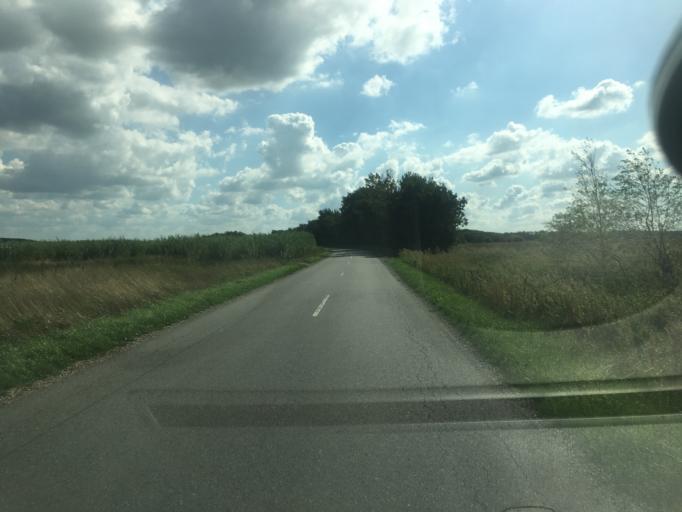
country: DE
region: Schleswig-Holstein
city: Ellhoft
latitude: 54.9643
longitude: 8.9621
